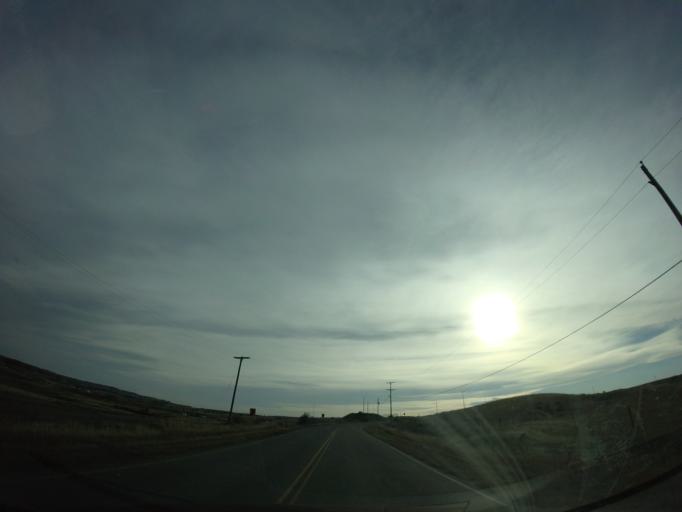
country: US
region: Montana
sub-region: Yellowstone County
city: Billings
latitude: 45.7900
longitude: -108.4554
